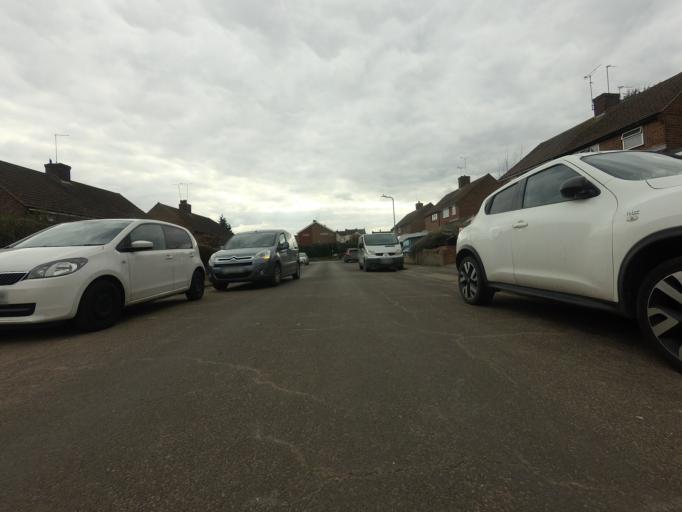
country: GB
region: England
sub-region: Kent
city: Swanley
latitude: 51.3959
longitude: 0.1807
